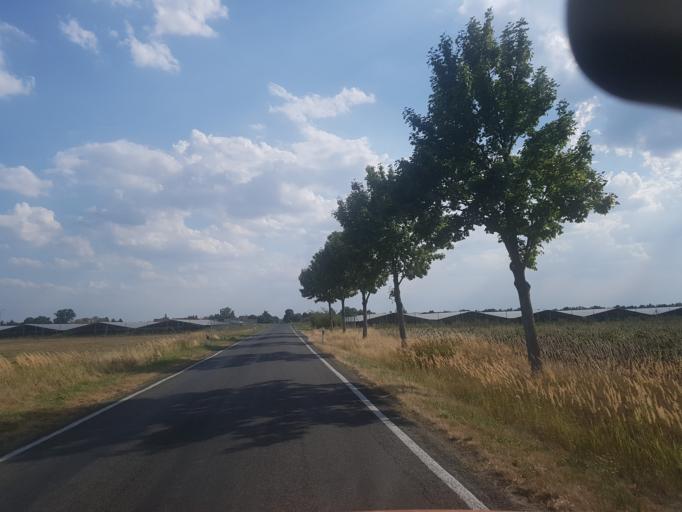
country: DE
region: Saxony-Anhalt
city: Holzdorf
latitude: 51.7815
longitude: 13.2142
